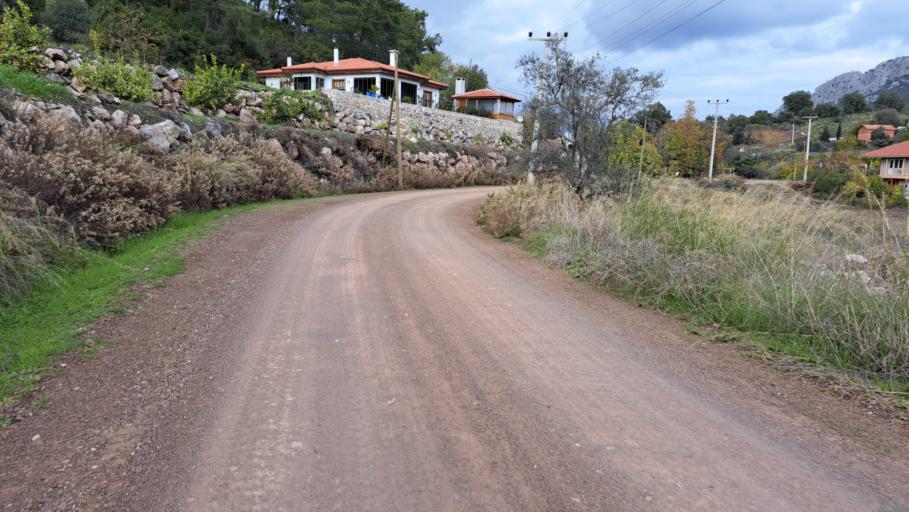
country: TR
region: Antalya
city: Tekirova
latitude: 36.4015
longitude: 30.4422
